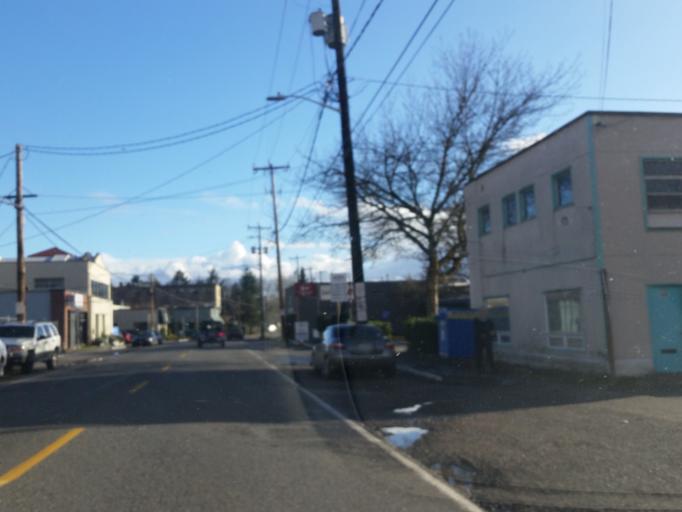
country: US
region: Washington
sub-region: King County
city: Seattle
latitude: 47.6628
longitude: -122.2945
